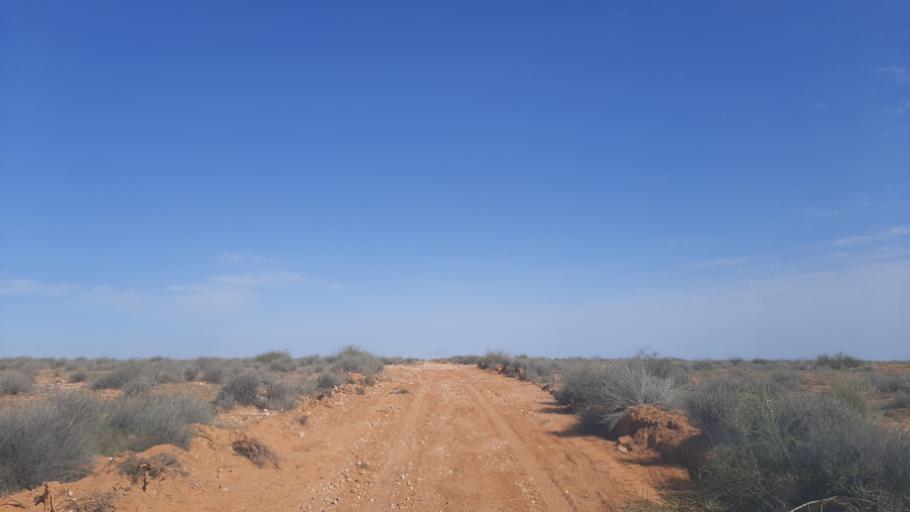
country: TN
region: Madanin
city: Medenine
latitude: 33.2451
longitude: 10.7433
